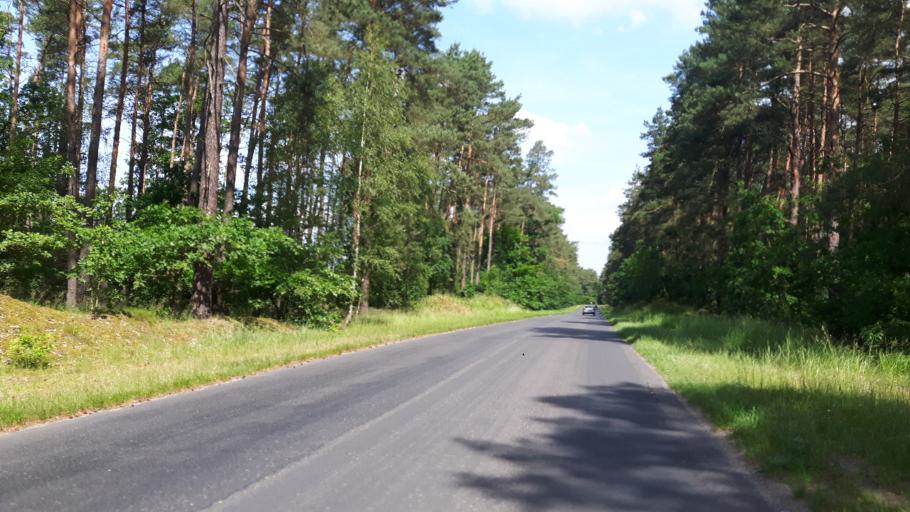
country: PL
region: West Pomeranian Voivodeship
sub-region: Powiat goleniowski
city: Goleniow
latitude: 53.5144
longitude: 14.7882
